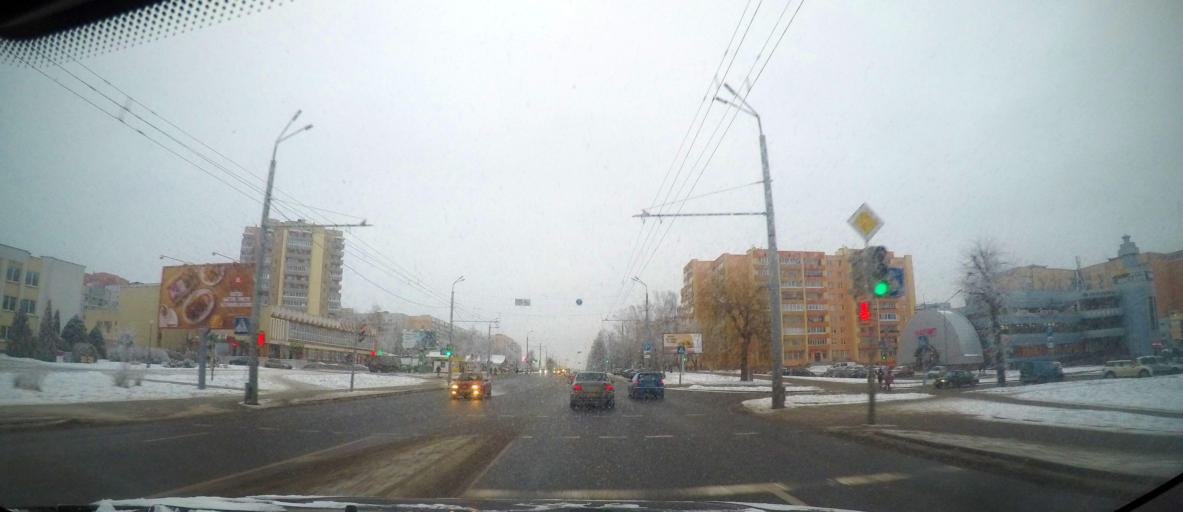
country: BY
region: Grodnenskaya
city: Hrodna
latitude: 53.6567
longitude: 23.8429
